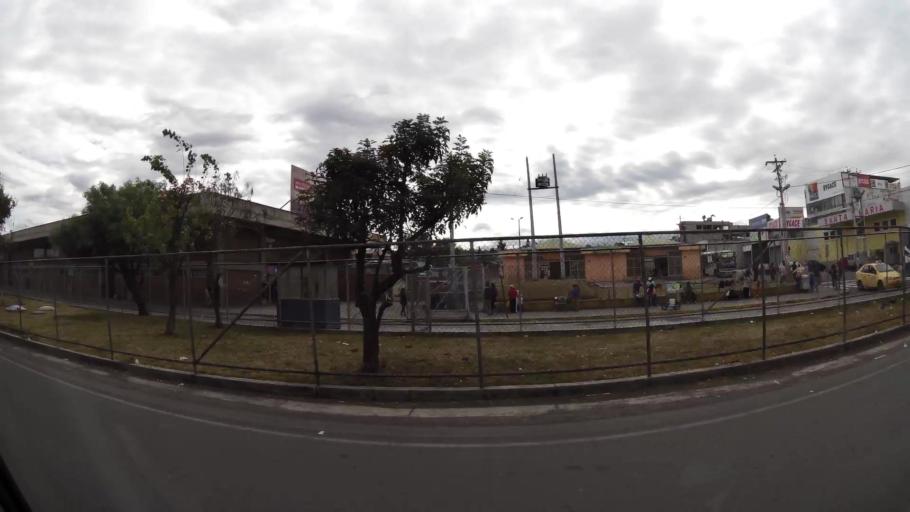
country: EC
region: Cotopaxi
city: Latacunga
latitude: -0.9340
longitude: -78.6205
